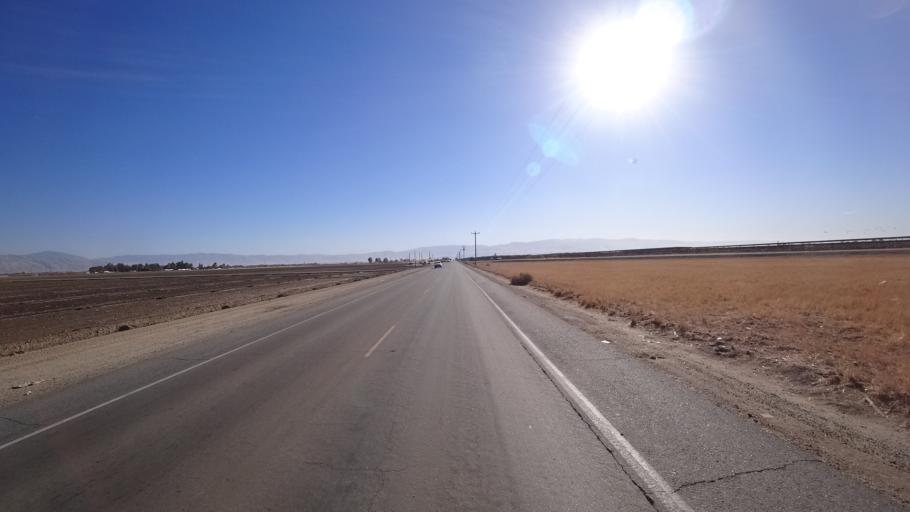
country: US
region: California
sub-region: Kern County
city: Greenfield
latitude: 35.2787
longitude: -118.9854
